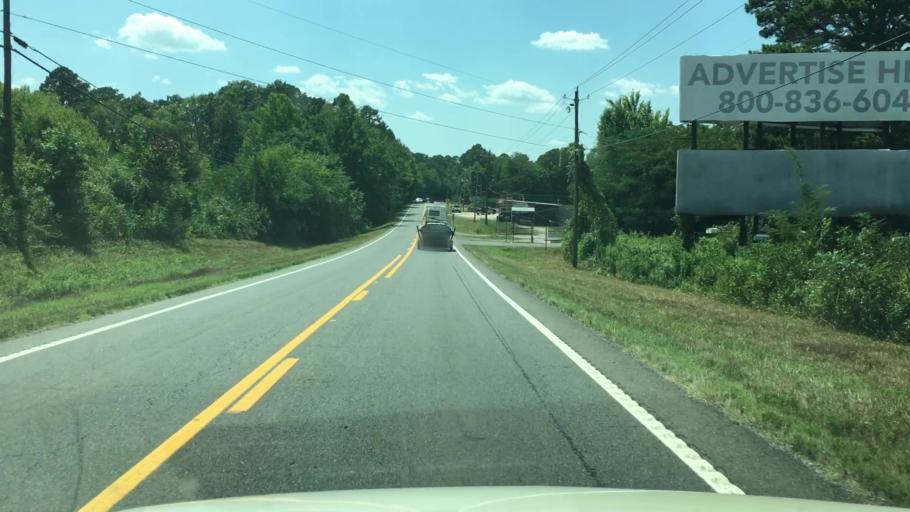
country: US
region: Arkansas
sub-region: Garland County
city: Piney
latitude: 34.5095
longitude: -93.1617
